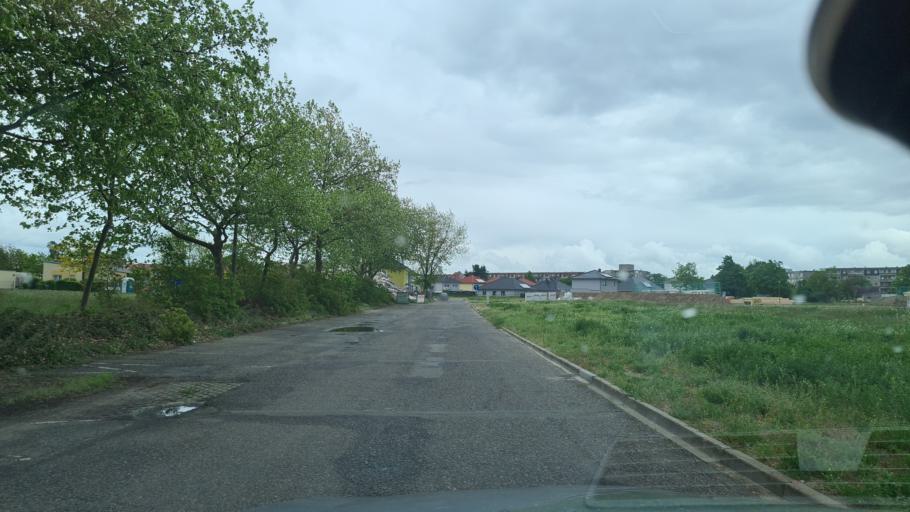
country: DE
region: Brandenburg
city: Eisenhuettenstadt
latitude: 52.1425
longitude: 14.6614
